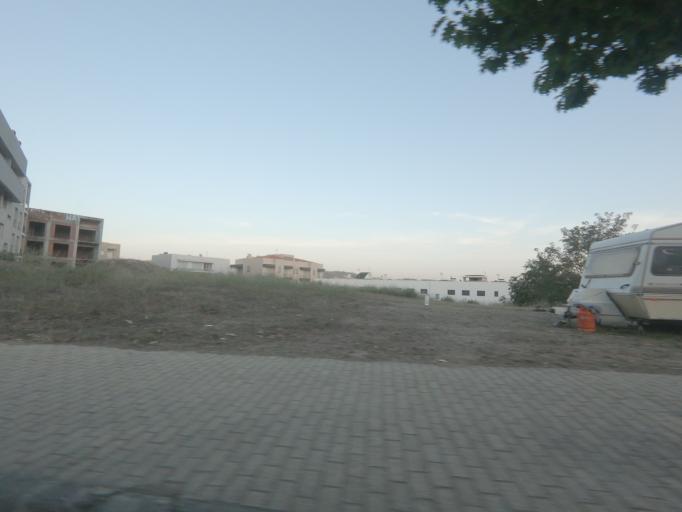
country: PT
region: Vila Real
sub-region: Vila Real
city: Vila Real
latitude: 41.3082
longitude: -7.7397
